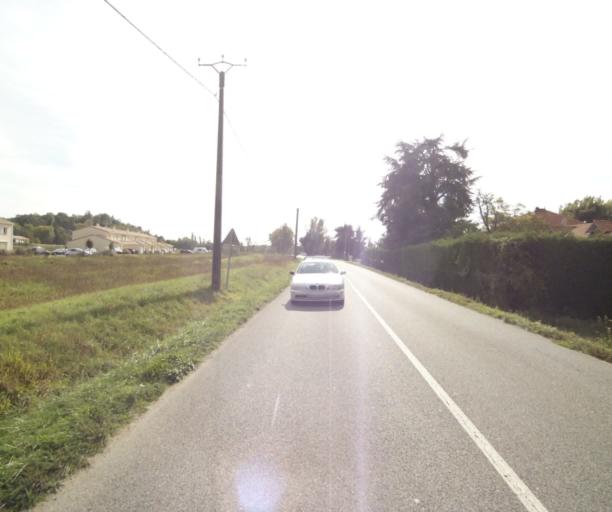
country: FR
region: Midi-Pyrenees
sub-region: Departement du Tarn-et-Garonne
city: Corbarieu
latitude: 43.9490
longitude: 1.3648
